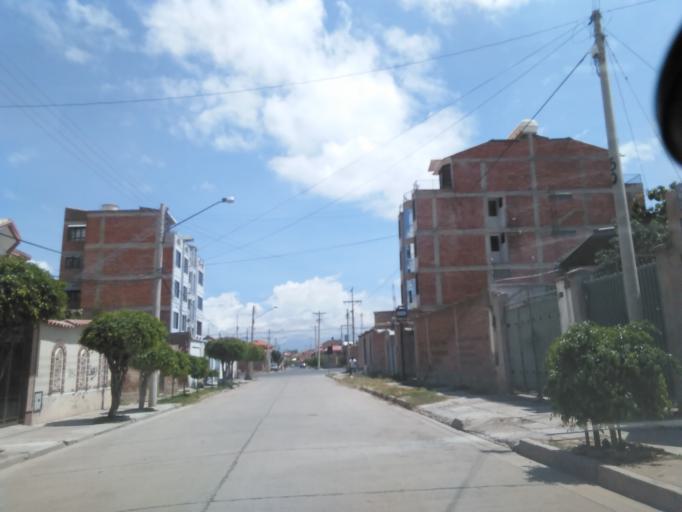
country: BO
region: Cochabamba
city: Cochabamba
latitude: -17.4161
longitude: -66.1648
